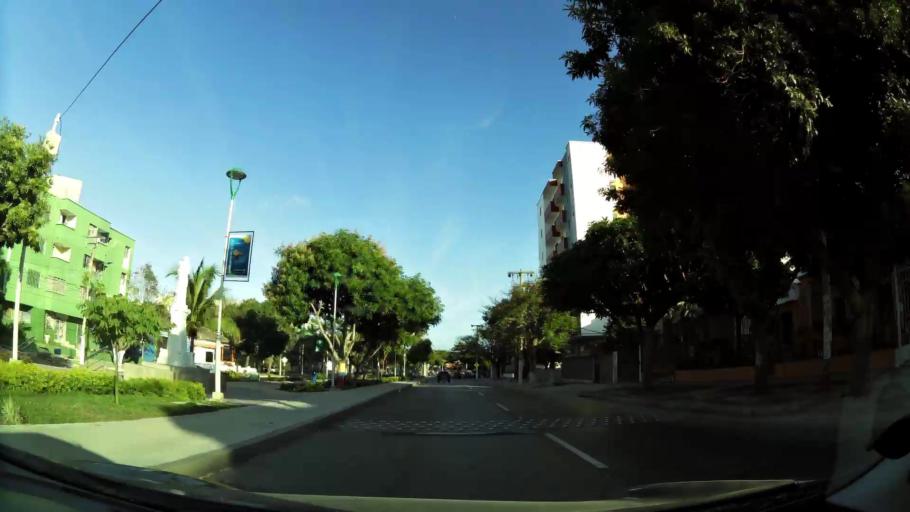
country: CO
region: Atlantico
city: Barranquilla
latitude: 10.9842
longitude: -74.7970
